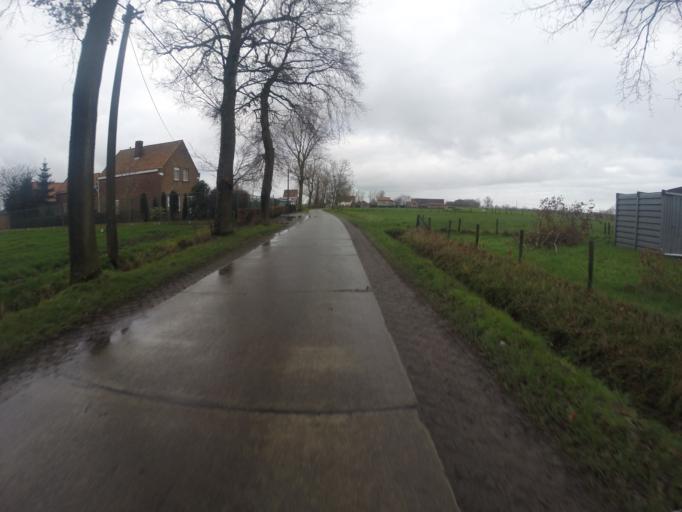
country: BE
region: Flanders
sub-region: Provincie Oost-Vlaanderen
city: Maldegem
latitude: 51.1723
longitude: 3.4945
